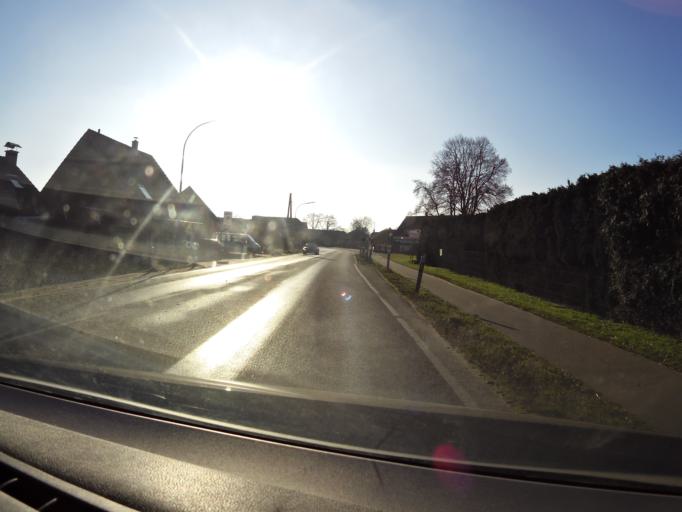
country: DE
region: North Rhine-Westphalia
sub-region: Regierungsbezirk Dusseldorf
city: Bruggen
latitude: 51.2579
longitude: 6.1850
